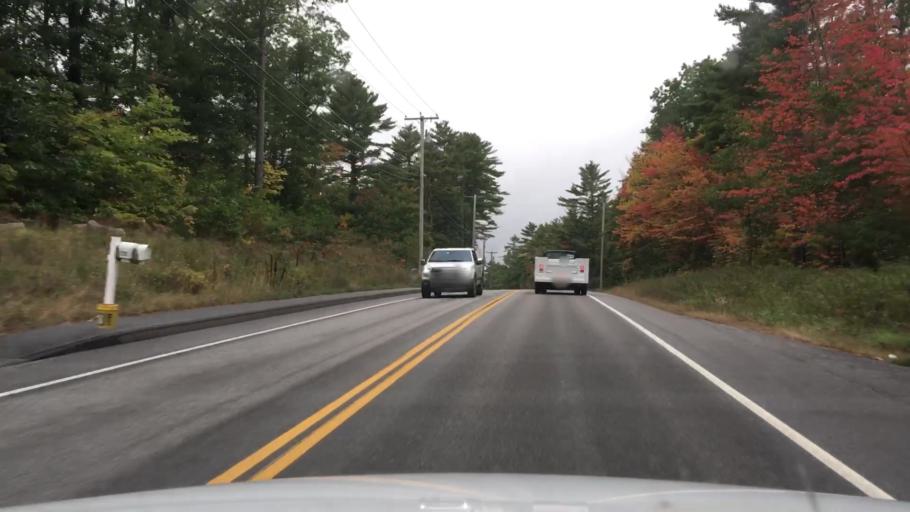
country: US
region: Maine
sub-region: Androscoggin County
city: Poland
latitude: 44.0659
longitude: -70.4000
